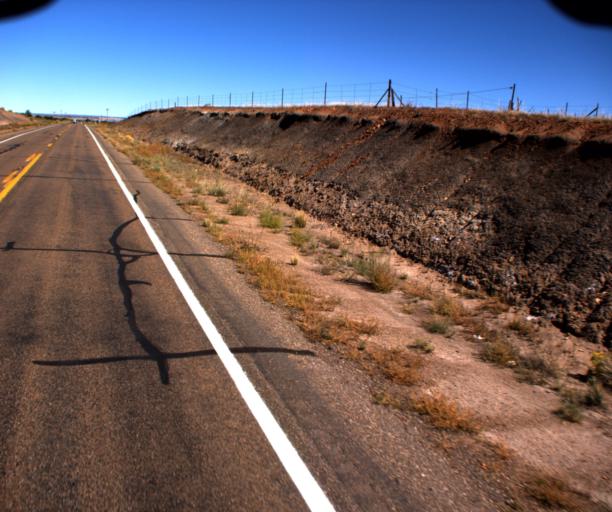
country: US
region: Arizona
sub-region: Apache County
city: Saint Johns
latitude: 34.4613
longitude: -109.4002
